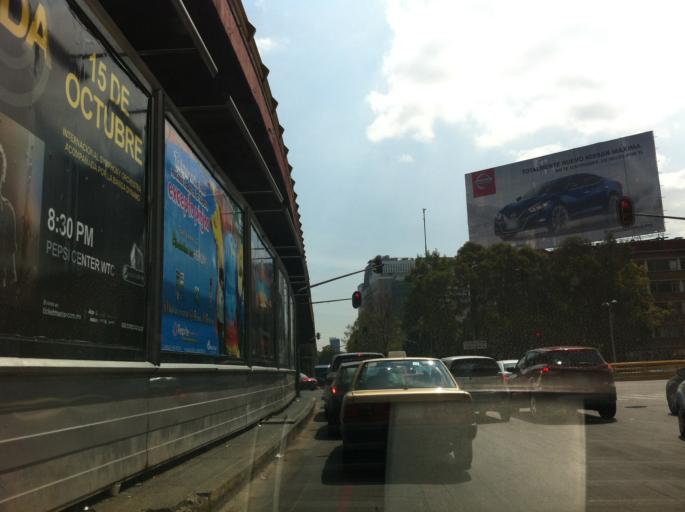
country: MX
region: Mexico City
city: Cuauhtemoc
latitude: 19.4364
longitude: -99.1703
